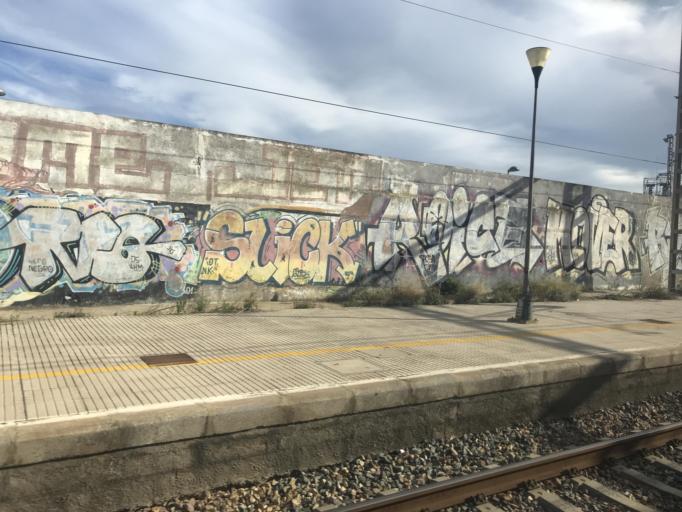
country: ES
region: Valencia
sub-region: Provincia de Castello
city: Benicarlo
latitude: 40.4290
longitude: 0.4163
